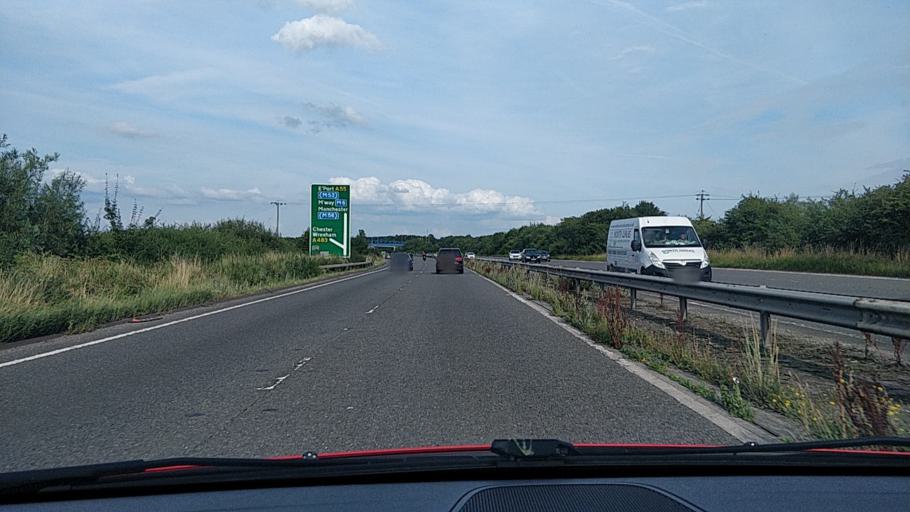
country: GB
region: England
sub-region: Cheshire West and Chester
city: Eccleston
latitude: 53.1561
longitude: -2.9227
